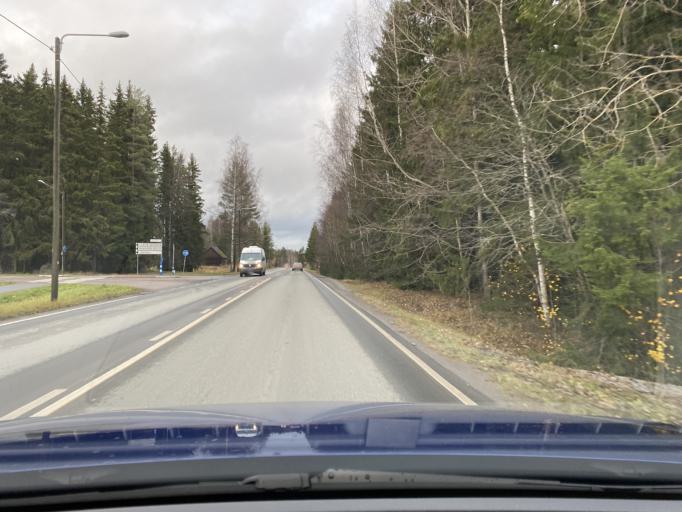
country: FI
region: Pirkanmaa
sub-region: Tampere
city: Lempaeaelae
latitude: 61.3414
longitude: 23.7544
